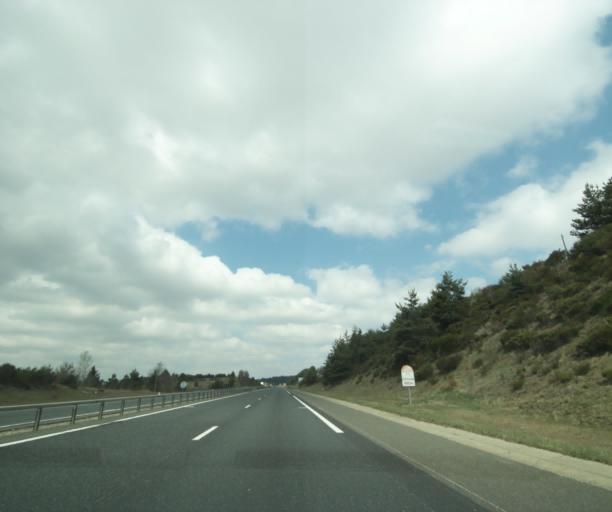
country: FR
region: Languedoc-Roussillon
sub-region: Departement de la Lozere
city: Aumont-Aubrac
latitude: 44.7571
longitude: 3.2869
